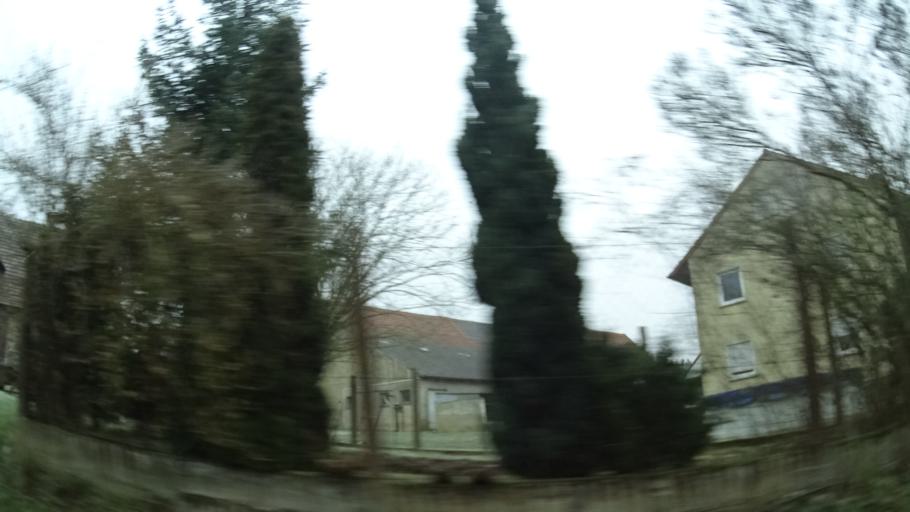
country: DE
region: Bavaria
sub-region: Regierungsbezirk Unterfranken
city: Sulzfeld am Main
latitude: 49.7043
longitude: 10.1295
